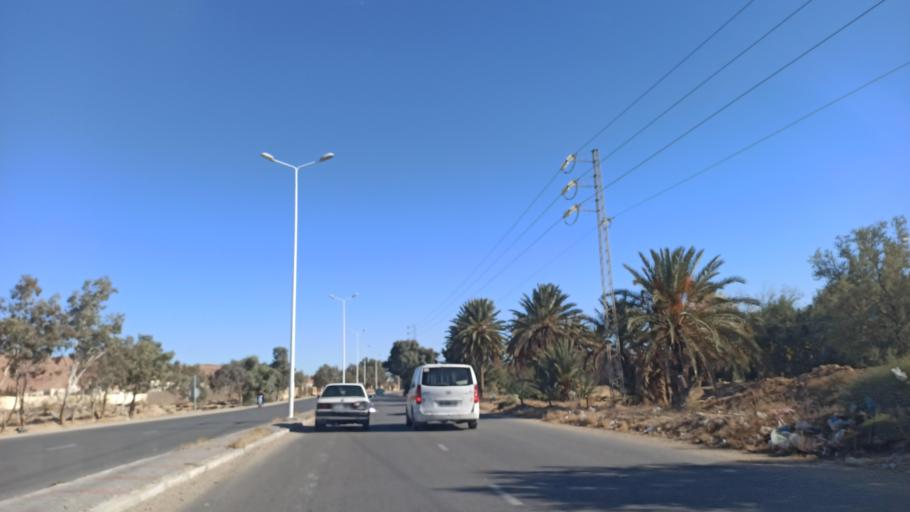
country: TN
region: Gafsa
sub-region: Gafsa Municipality
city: Gafsa
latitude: 34.4221
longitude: 8.7480
